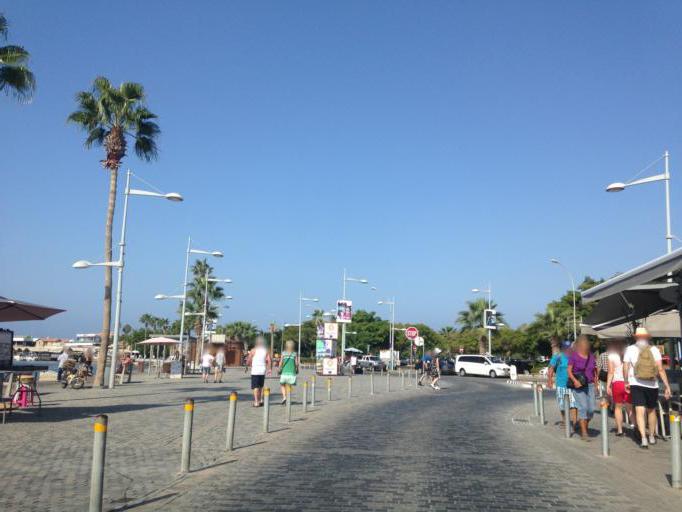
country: CY
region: Pafos
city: Paphos
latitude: 34.7558
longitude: 32.4115
